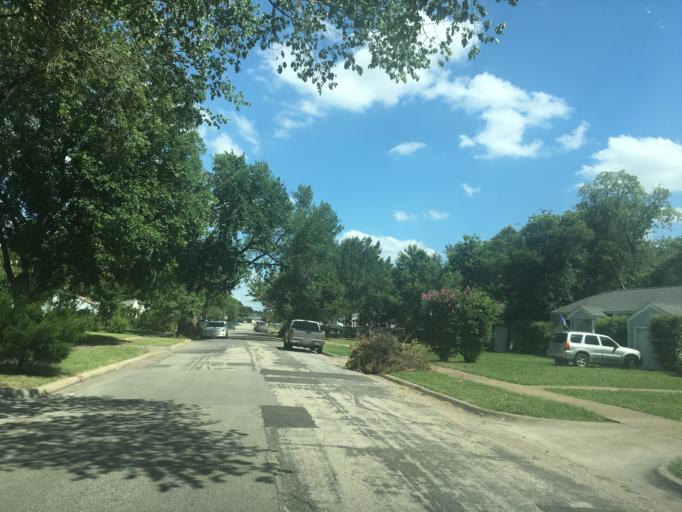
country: US
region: Texas
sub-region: Dallas County
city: Garland
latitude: 32.8398
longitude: -96.6926
